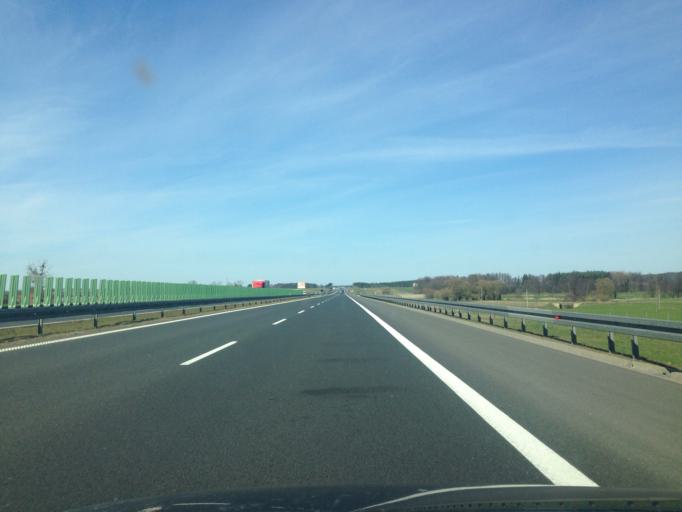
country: PL
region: Pomeranian Voivodeship
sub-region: Powiat starogardzki
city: Smetowo Graniczne
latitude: 53.7659
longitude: 18.6346
